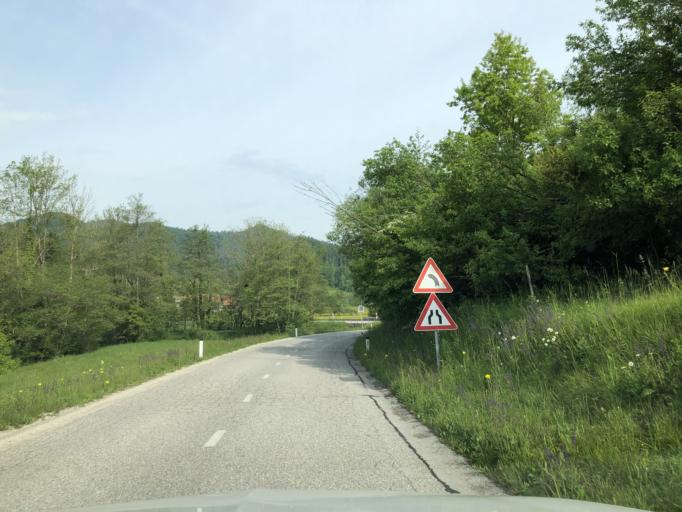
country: SI
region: Velike Lasce
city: Velike Lasce
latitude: 45.8081
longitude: 14.6125
